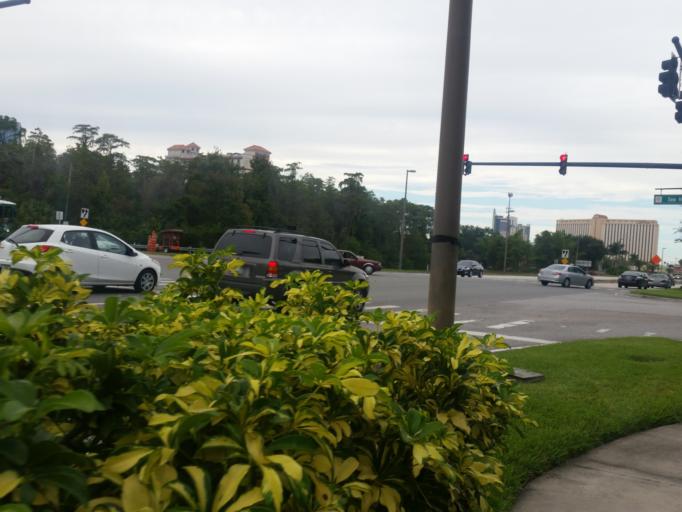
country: US
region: Florida
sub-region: Orange County
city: Williamsburg
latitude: 28.4156
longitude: -81.4589
